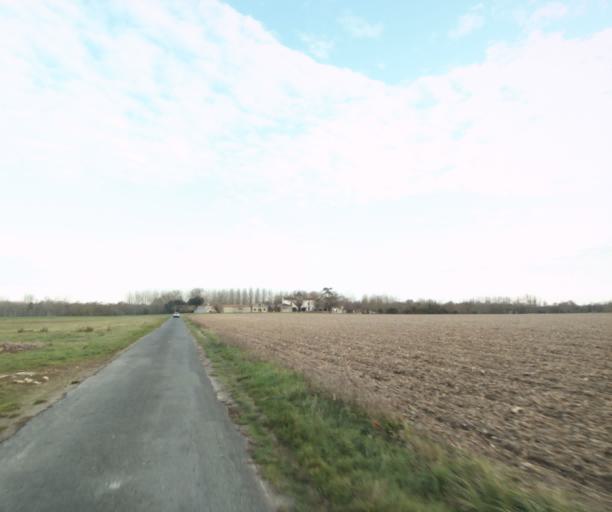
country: FR
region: Poitou-Charentes
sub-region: Departement de la Charente-Maritime
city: Les Gonds
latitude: 45.7095
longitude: -0.6072
